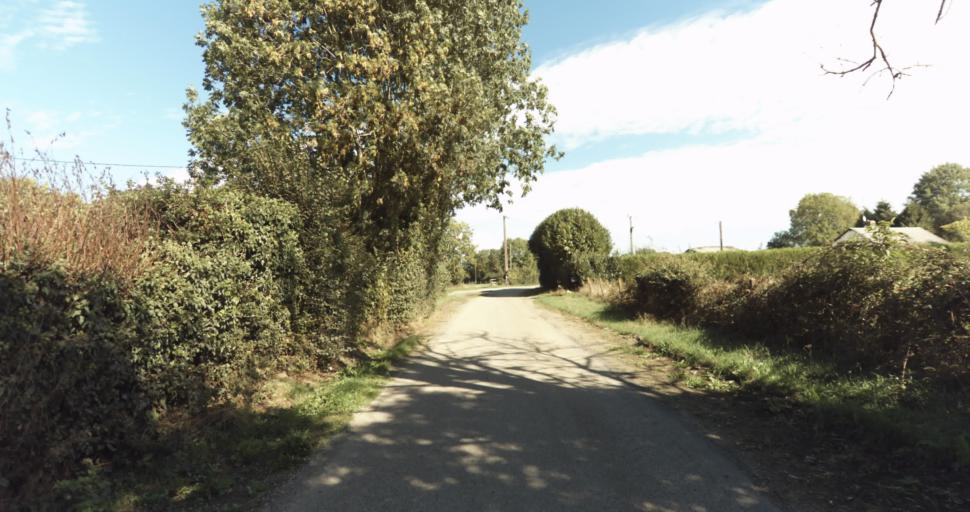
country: FR
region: Lower Normandy
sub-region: Departement de l'Orne
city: Gace
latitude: 48.7962
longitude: 0.2321
